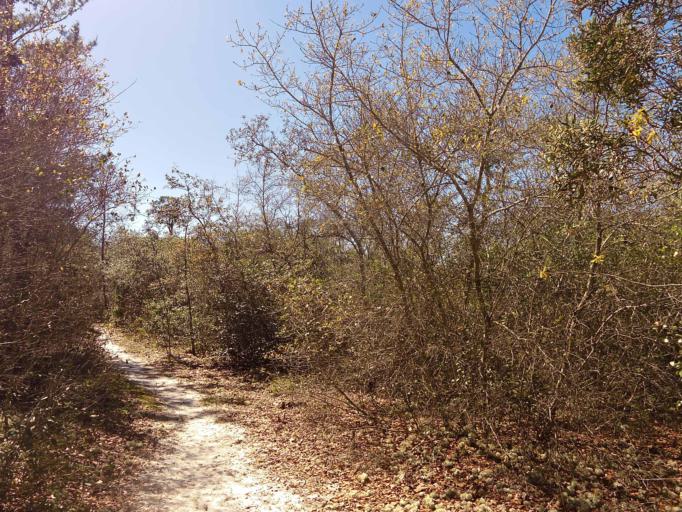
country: US
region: Florida
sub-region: Clay County
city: Keystone Heights
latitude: 29.8385
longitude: -81.9856
